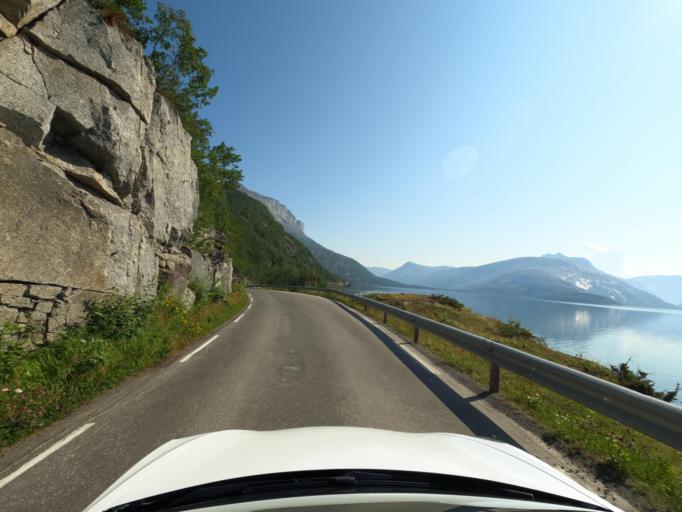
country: NO
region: Nordland
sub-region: Narvik
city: Narvik
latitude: 68.2909
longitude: 17.3596
